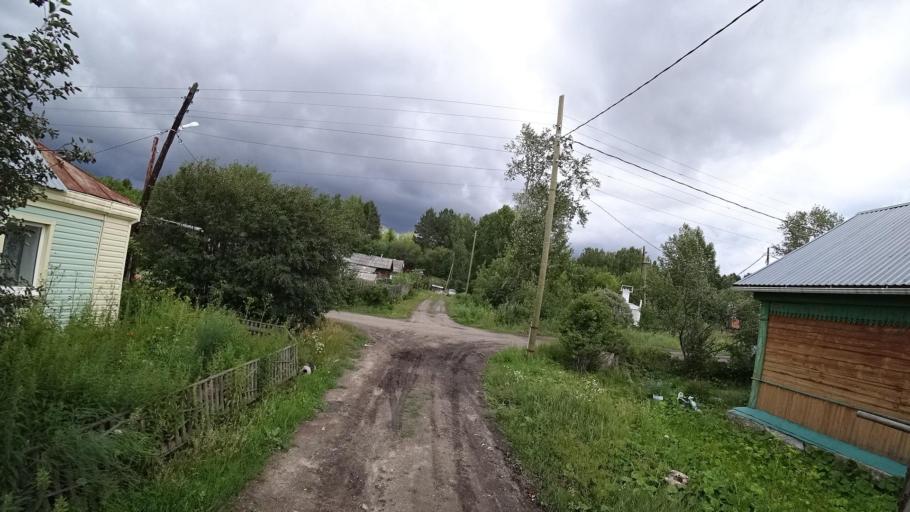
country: RU
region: Sverdlovsk
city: Kamyshlov
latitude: 56.8587
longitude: 62.7183
